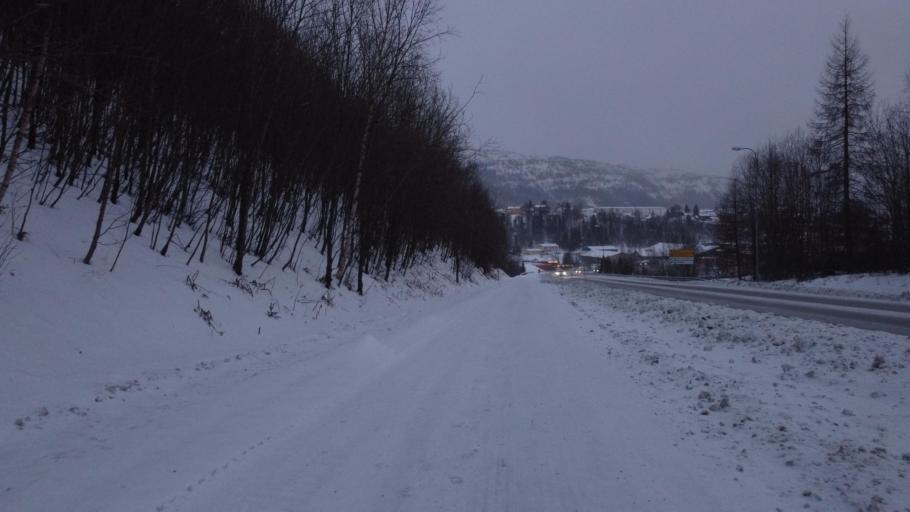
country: NO
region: Nordland
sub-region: Rana
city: Mo i Rana
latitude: 66.3216
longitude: 14.1566
